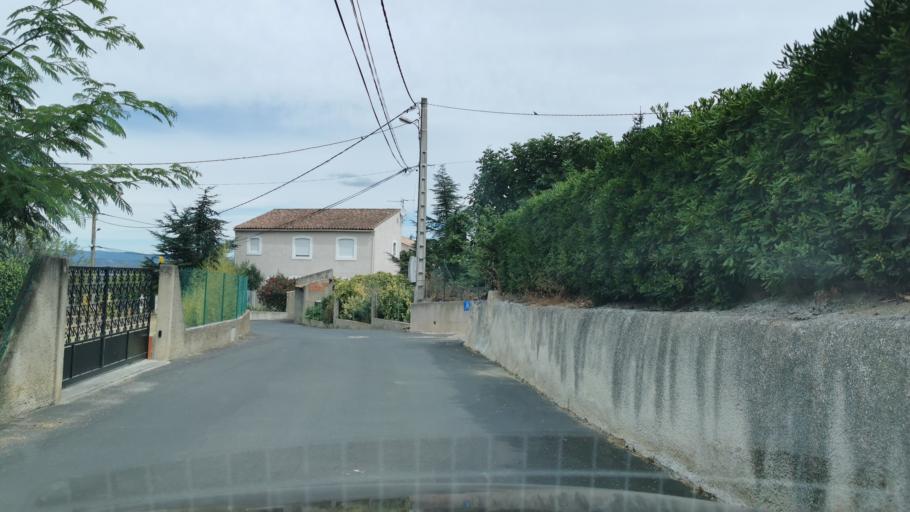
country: FR
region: Languedoc-Roussillon
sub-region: Departement de l'Aude
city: Marcorignan
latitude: 43.2250
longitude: 2.9266
